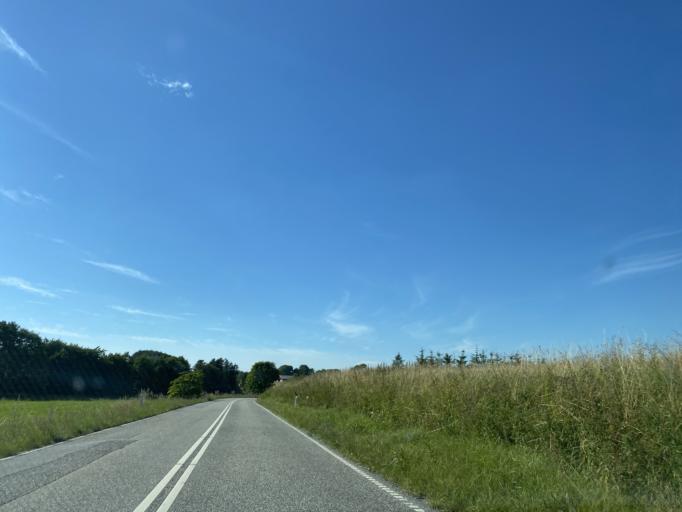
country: DK
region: Central Jutland
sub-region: Hedensted Kommune
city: Torring
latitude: 55.8242
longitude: 9.4428
